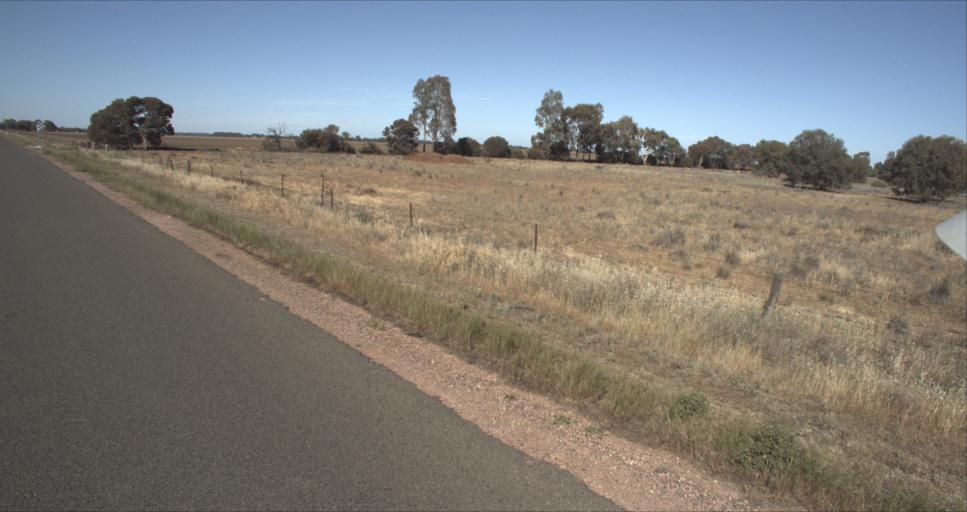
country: AU
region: New South Wales
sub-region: Leeton
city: Leeton
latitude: -34.5660
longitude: 146.2644
